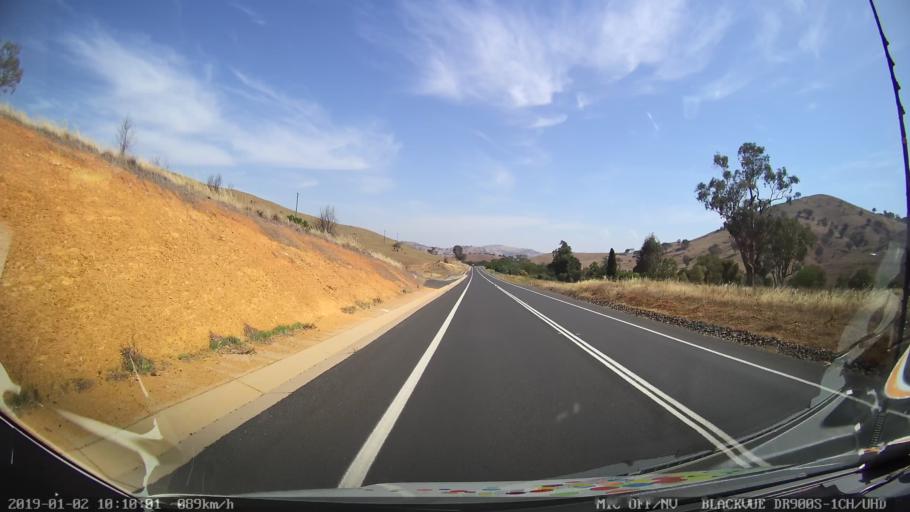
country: AU
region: New South Wales
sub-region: Gundagai
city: Gundagai
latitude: -35.1096
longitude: 148.0971
